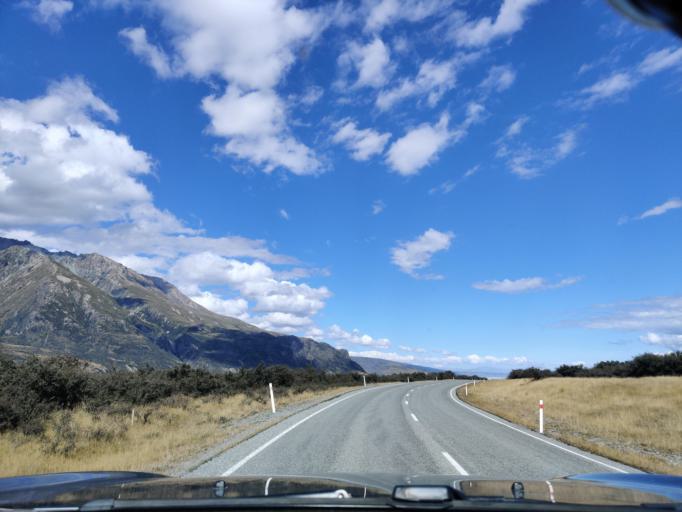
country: NZ
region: Canterbury
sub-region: Timaru District
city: Pleasant Point
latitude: -43.7611
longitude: 170.1216
